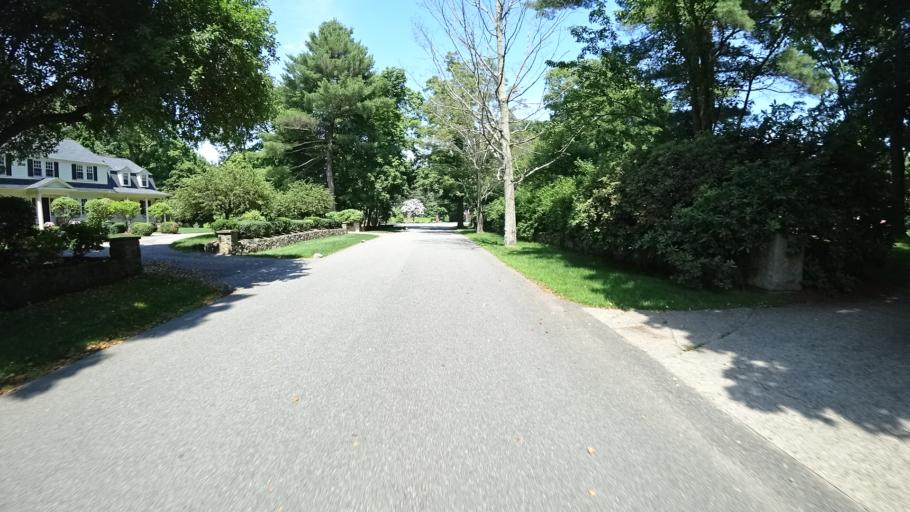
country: US
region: Massachusetts
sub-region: Norfolk County
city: Dedham
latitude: 42.2531
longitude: -71.1881
